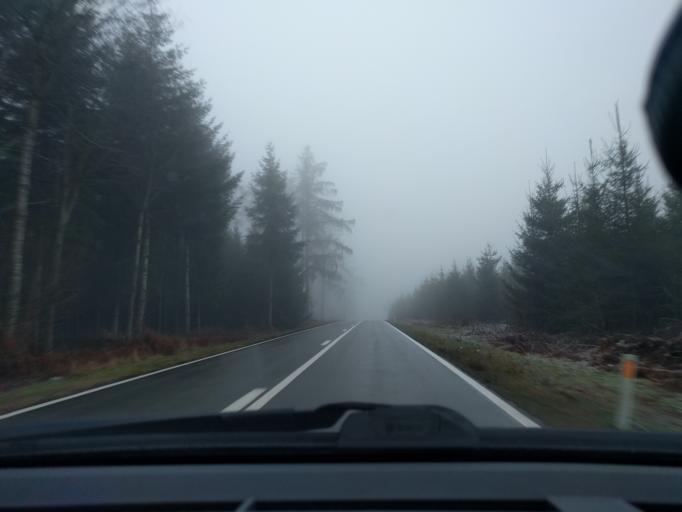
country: BE
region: Wallonia
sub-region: Province du Luxembourg
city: Gouvy
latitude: 50.2048
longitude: 5.9738
